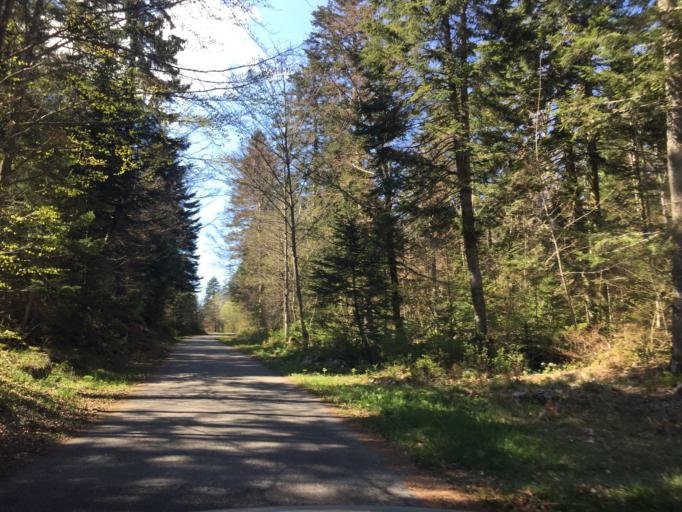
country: FR
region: Rhone-Alpes
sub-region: Departement de la Savoie
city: Novalaise
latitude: 45.5946
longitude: 5.8158
